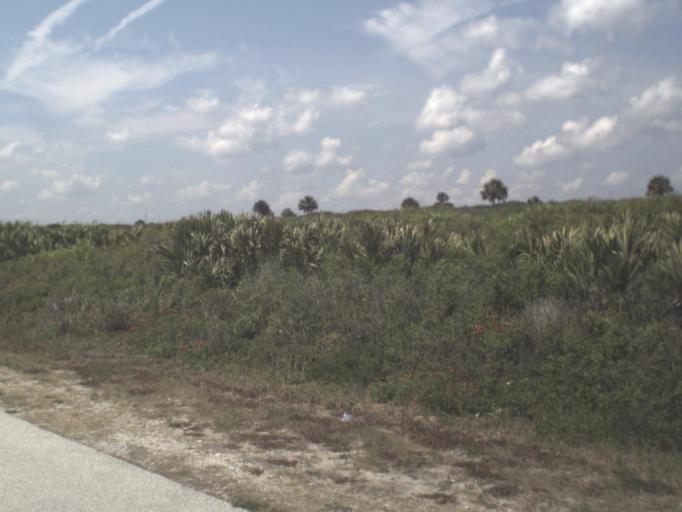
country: US
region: Florida
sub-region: Saint Johns County
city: Villano Beach
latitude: 30.0363
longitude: -81.3268
